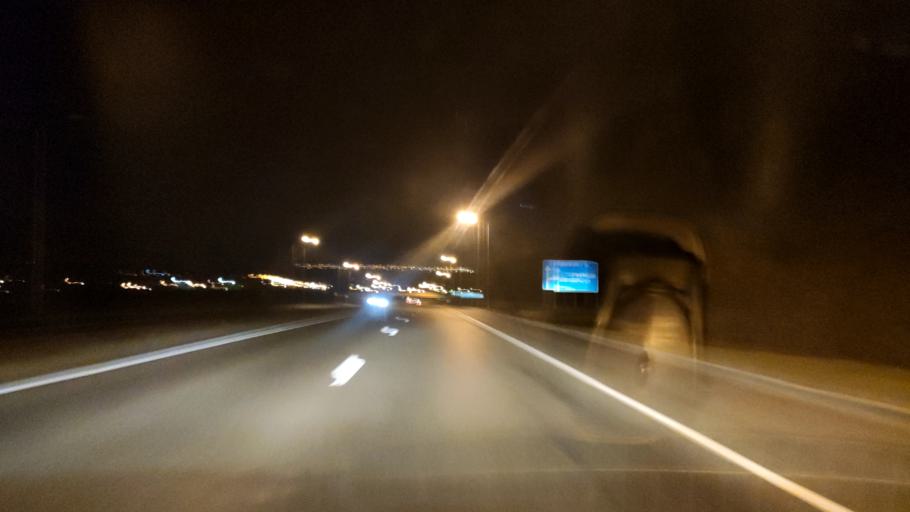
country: RU
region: Belgorod
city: Staryy Oskol
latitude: 51.3395
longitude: 37.7893
